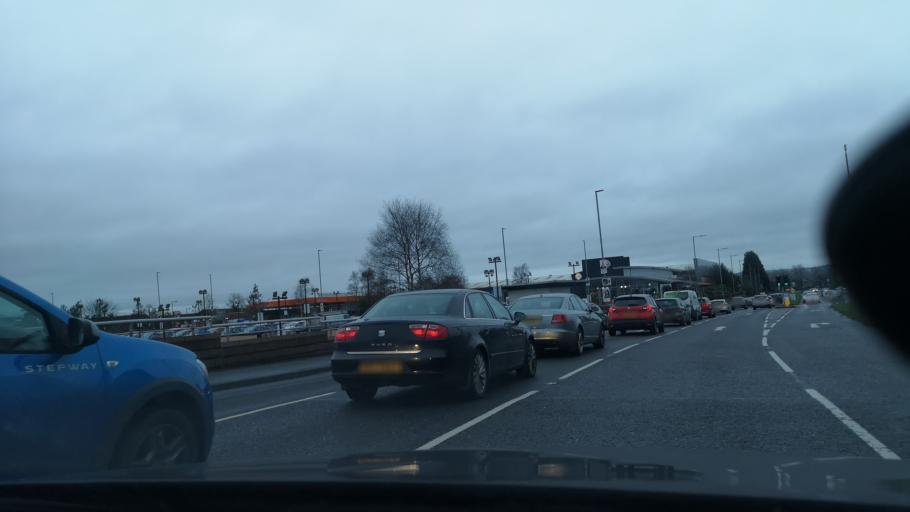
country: GB
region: Northern Ireland
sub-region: Castlereagh District
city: Castlereagh
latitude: 54.5635
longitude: -5.9074
